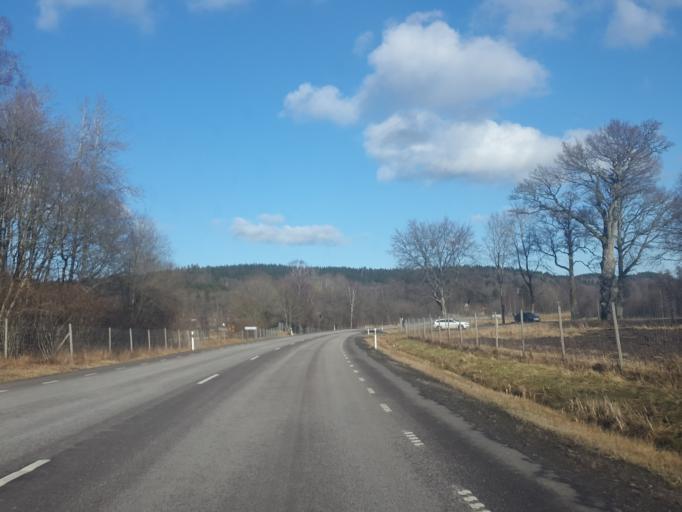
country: SE
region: Vaestra Goetaland
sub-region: Alingsas Kommun
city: Ingared
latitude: 57.9596
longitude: 12.3986
